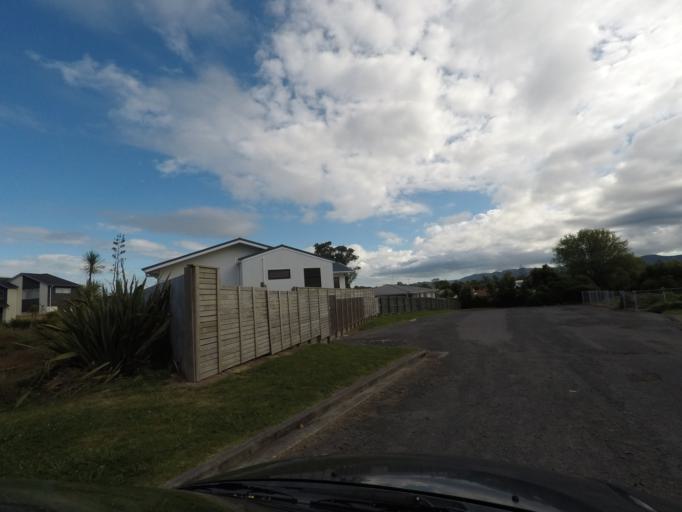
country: NZ
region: Auckland
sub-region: Auckland
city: Rosebank
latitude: -36.8742
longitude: 174.6431
